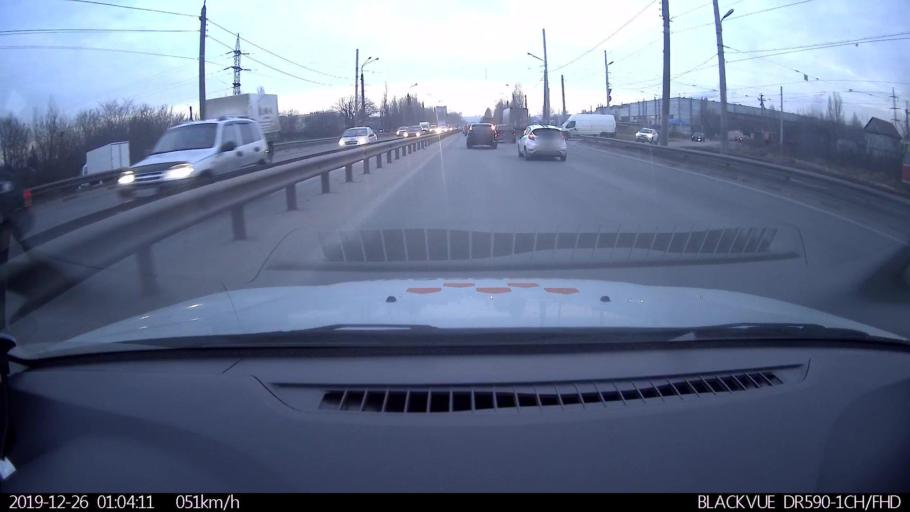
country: RU
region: Nizjnij Novgorod
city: Nizhniy Novgorod
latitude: 56.2809
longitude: 43.8979
